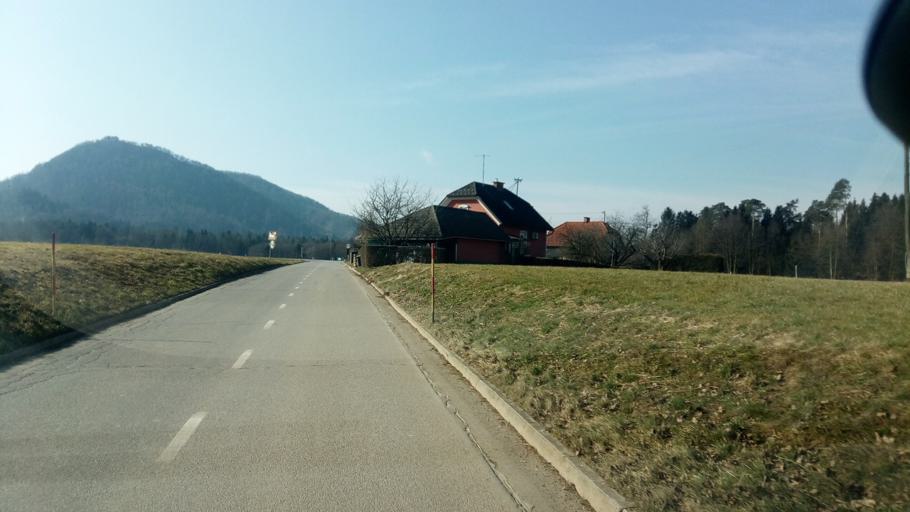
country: SI
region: Vodice
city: Vodice
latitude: 46.1478
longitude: 14.4823
